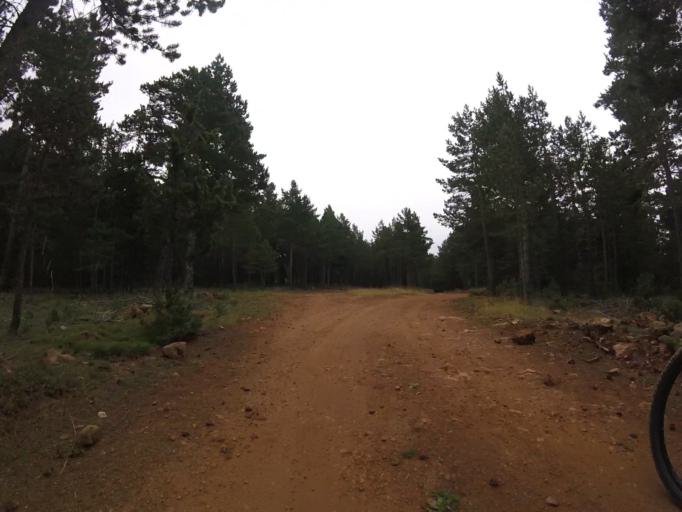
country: ES
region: Aragon
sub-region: Provincia de Teruel
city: Valdelinares
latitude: 40.3705
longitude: -0.6206
